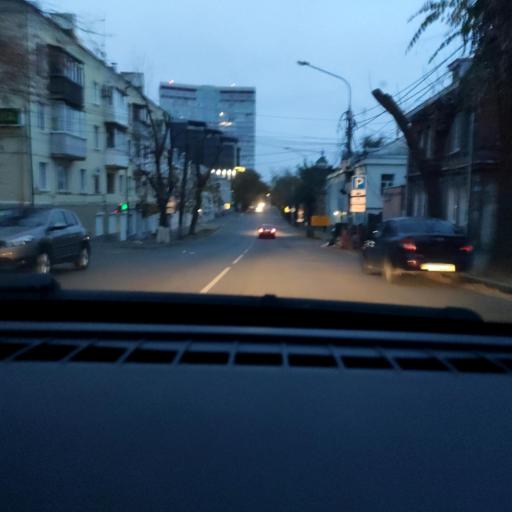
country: RU
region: Voronezj
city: Voronezh
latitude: 51.6744
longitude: 39.2163
